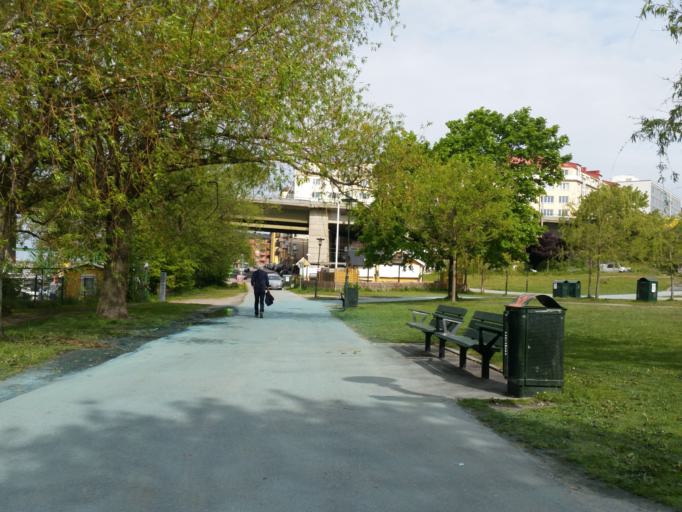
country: SE
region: Stockholm
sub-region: Stockholms Kommun
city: Arsta
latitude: 59.3135
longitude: 18.0356
